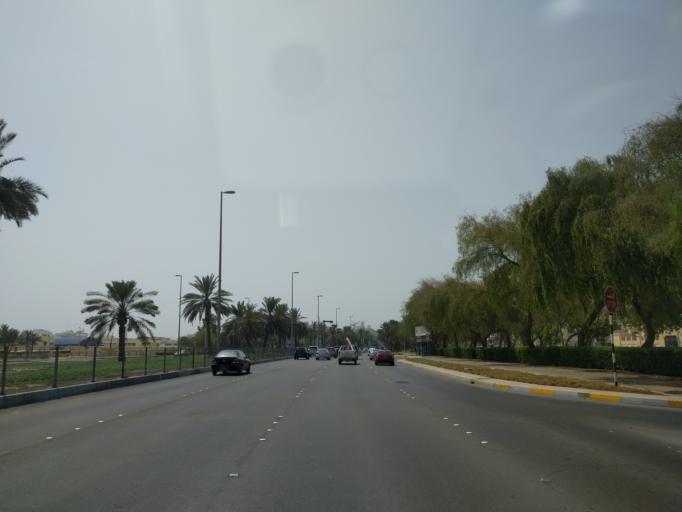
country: AE
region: Abu Dhabi
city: Abu Dhabi
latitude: 24.4427
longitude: 54.4053
